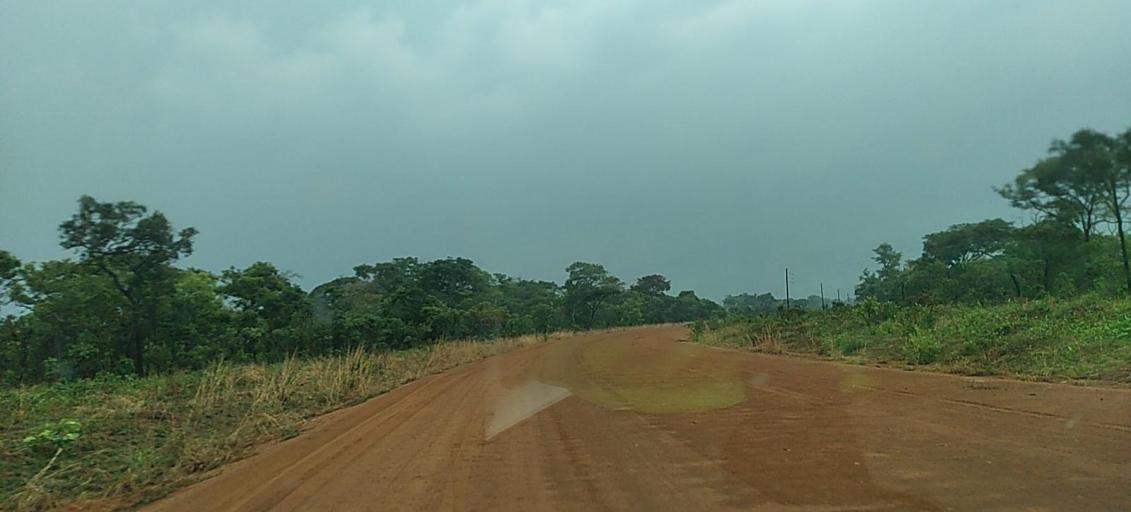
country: ZM
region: North-Western
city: Mwinilunga
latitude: -11.6210
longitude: 24.4026
